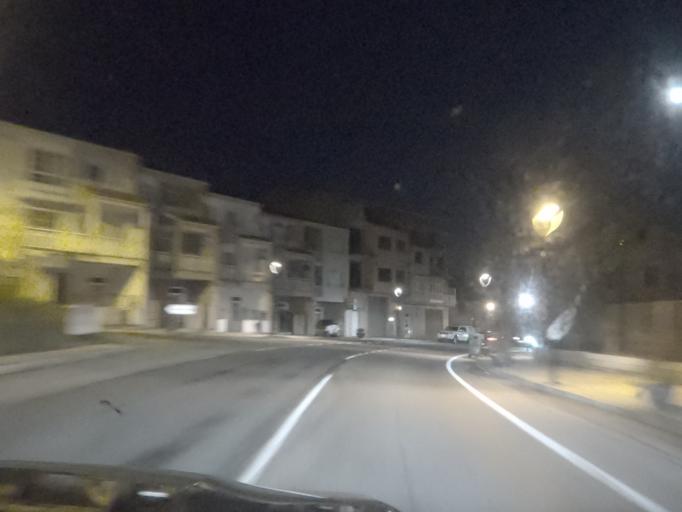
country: ES
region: Galicia
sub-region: Provincia de Ourense
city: Verin
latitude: 41.9398
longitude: -7.4455
